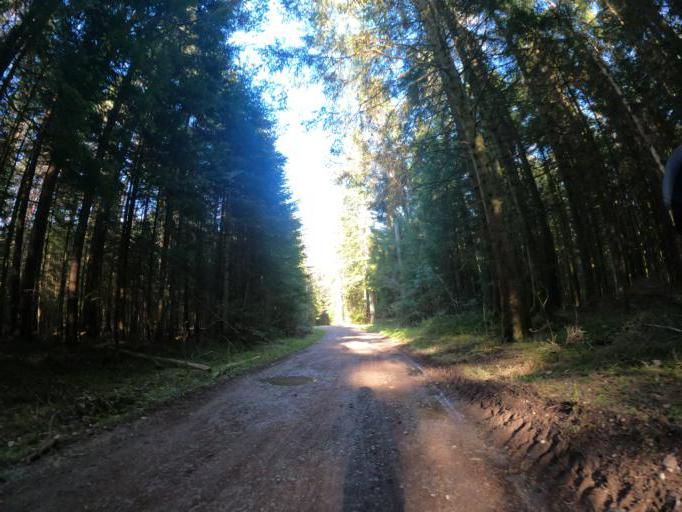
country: DE
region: Baden-Wuerttemberg
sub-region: Karlsruhe Region
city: Oberreichenbach
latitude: 48.7070
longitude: 8.6358
